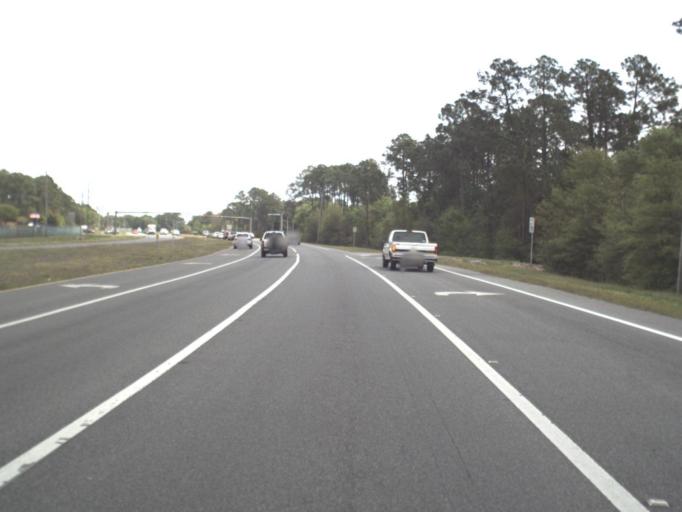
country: US
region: Florida
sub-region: Escambia County
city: Warrington
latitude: 30.3966
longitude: -87.2908
